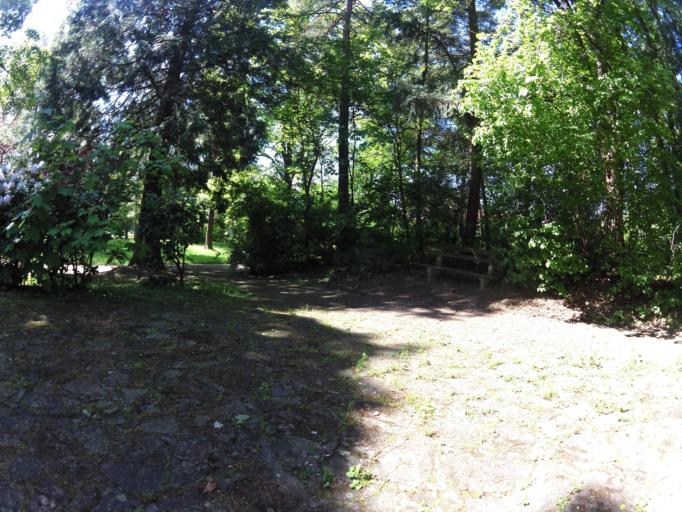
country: DE
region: Thuringia
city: Dankmarshausen
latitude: 50.9524
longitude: 10.0351
